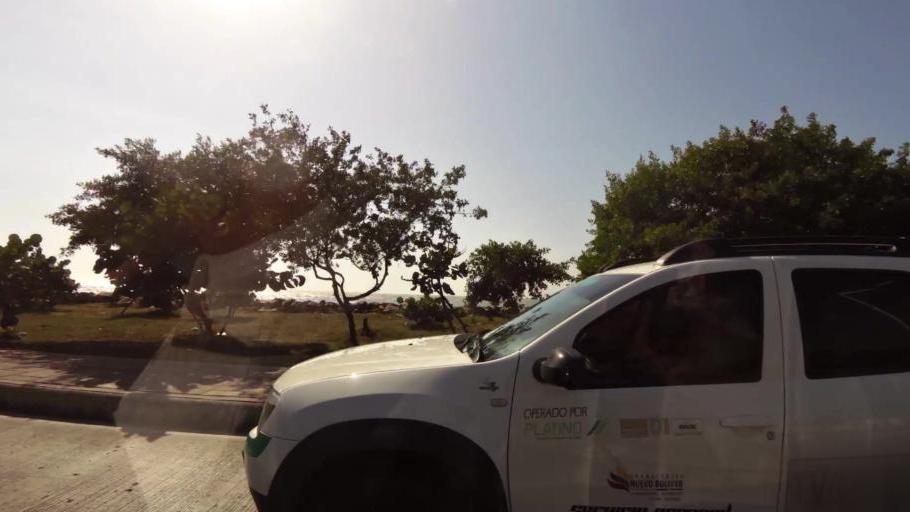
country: CO
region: Bolivar
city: Cartagena
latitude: 10.4148
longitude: -75.5511
